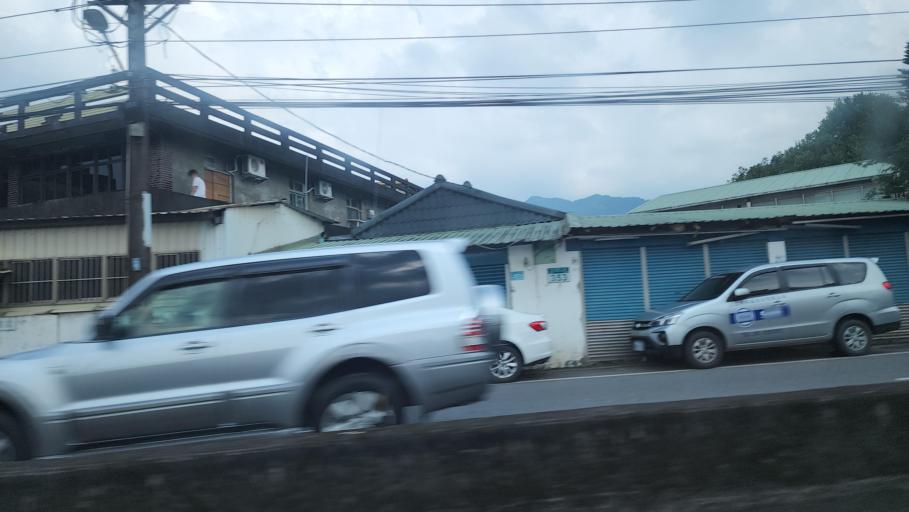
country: TW
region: Taiwan
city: Daxi
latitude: 24.9092
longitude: 121.3656
